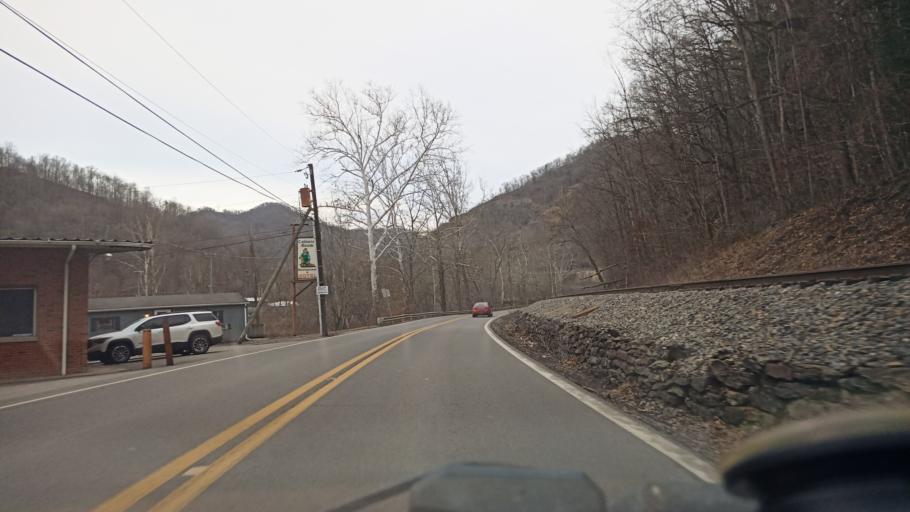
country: US
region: West Virginia
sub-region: Logan County
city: Mallory
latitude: 37.7275
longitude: -81.8754
